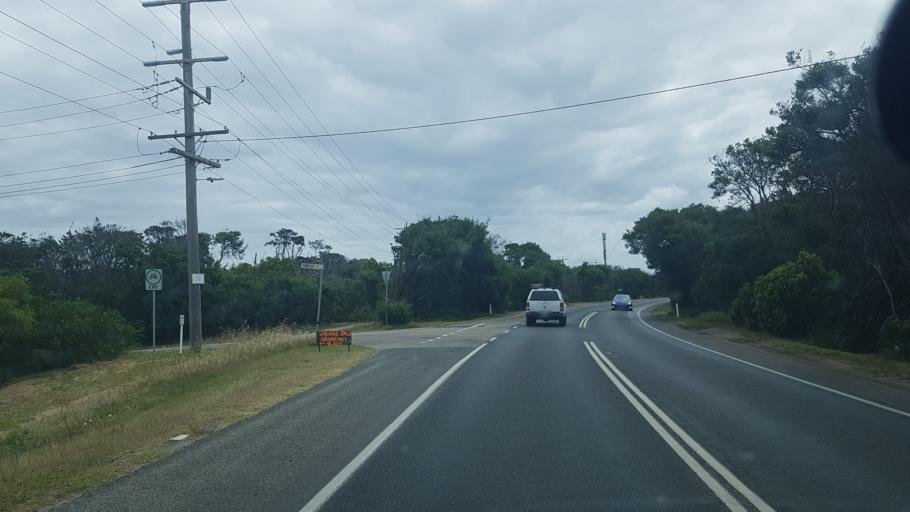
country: AU
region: Victoria
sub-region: Mornington Peninsula
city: Blairgowrie
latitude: -38.3782
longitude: 144.7824
